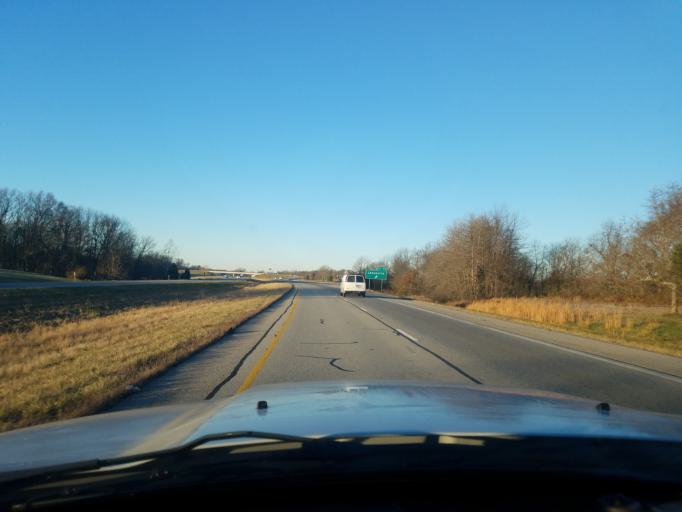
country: US
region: Indiana
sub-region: Floyd County
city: Georgetown
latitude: 38.2681
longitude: -85.9944
